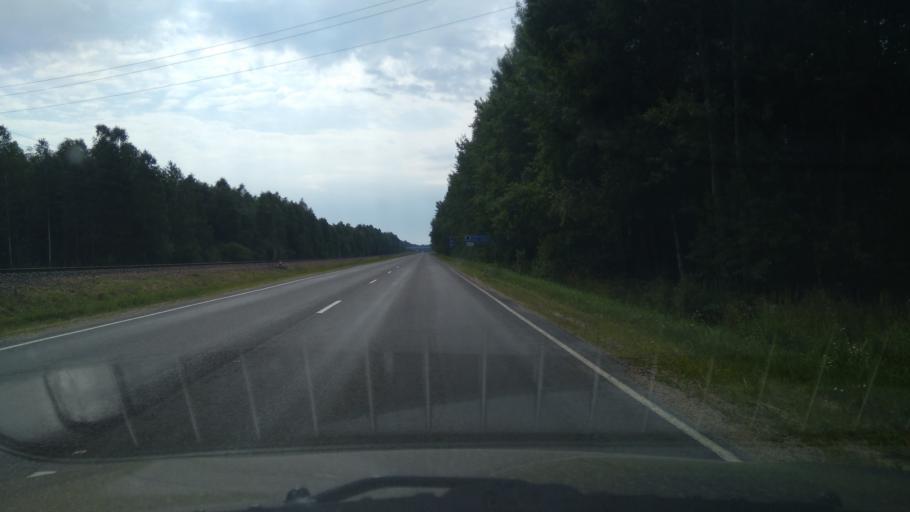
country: BY
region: Brest
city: Nyakhachava
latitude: 52.5837
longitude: 25.1008
